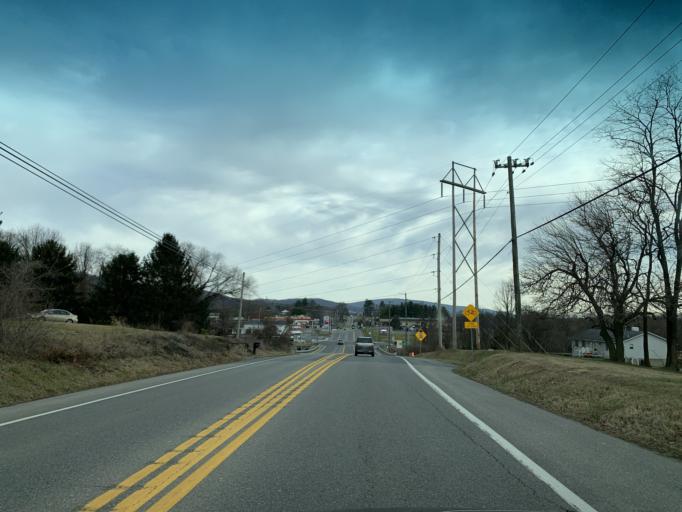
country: US
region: Maryland
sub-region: Washington County
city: Boonsboro
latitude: 39.5219
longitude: -77.6612
